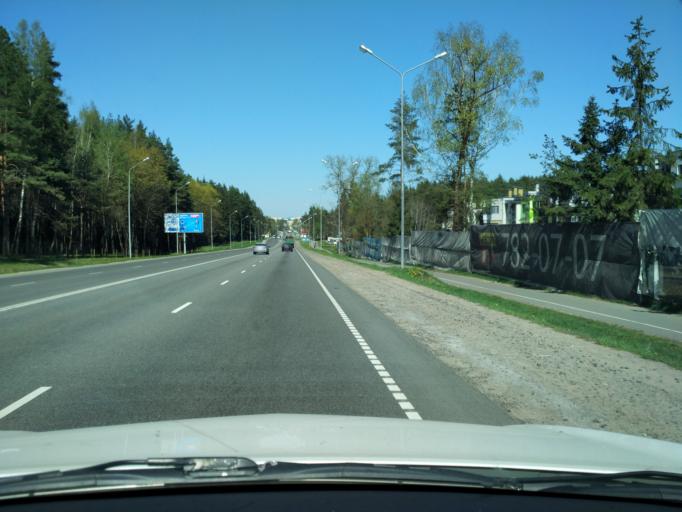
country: BY
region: Minsk
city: Borovlyany
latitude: 53.9853
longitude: 27.6602
